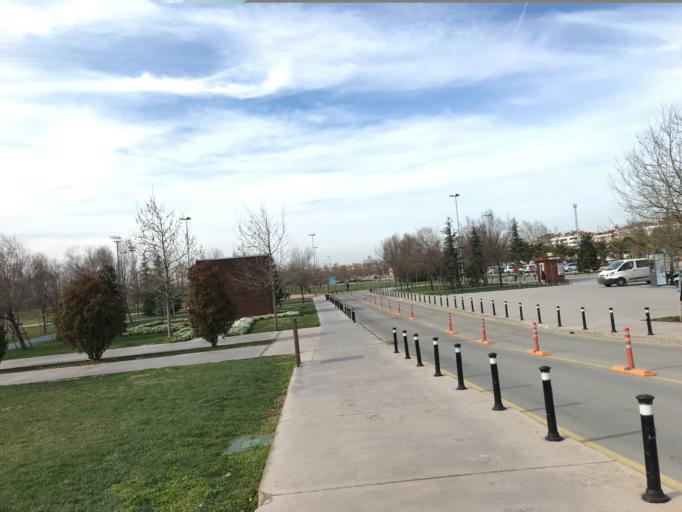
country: TR
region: Istanbul
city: Maltepe
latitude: 40.9331
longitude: 29.1156
